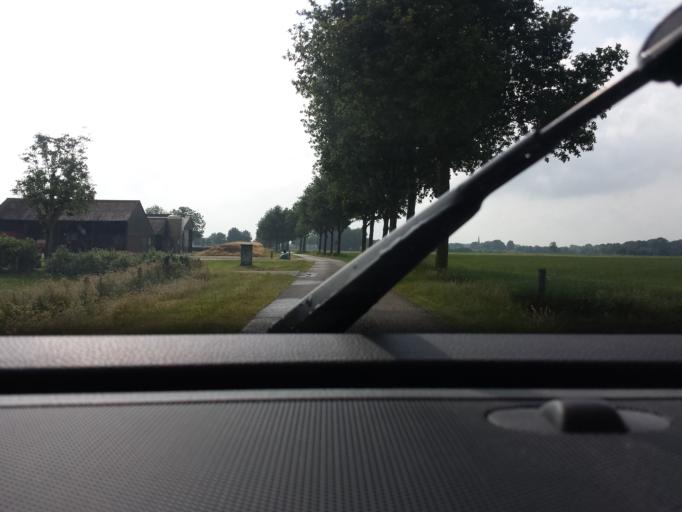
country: NL
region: Gelderland
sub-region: Berkelland
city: Eibergen
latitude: 52.0604
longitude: 6.5869
